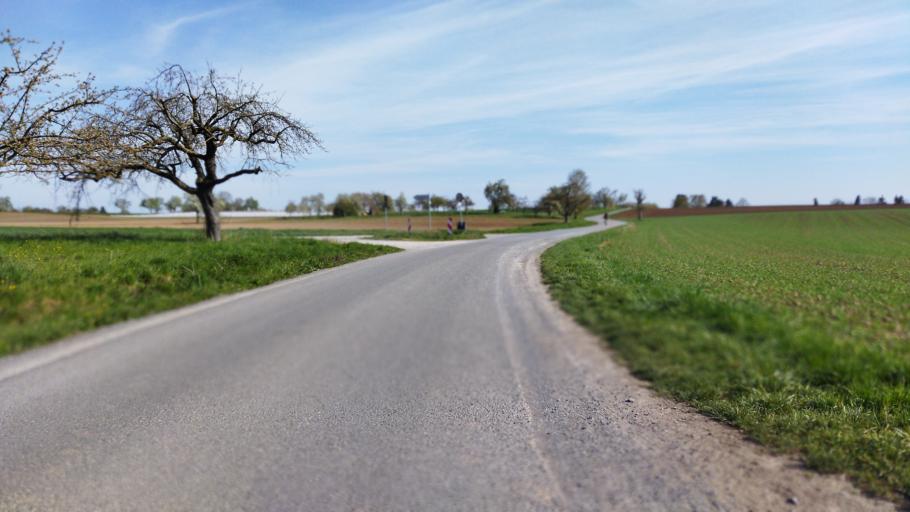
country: DE
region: Baden-Wuerttemberg
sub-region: Regierungsbezirk Stuttgart
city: Freudental
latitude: 48.9809
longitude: 9.0647
